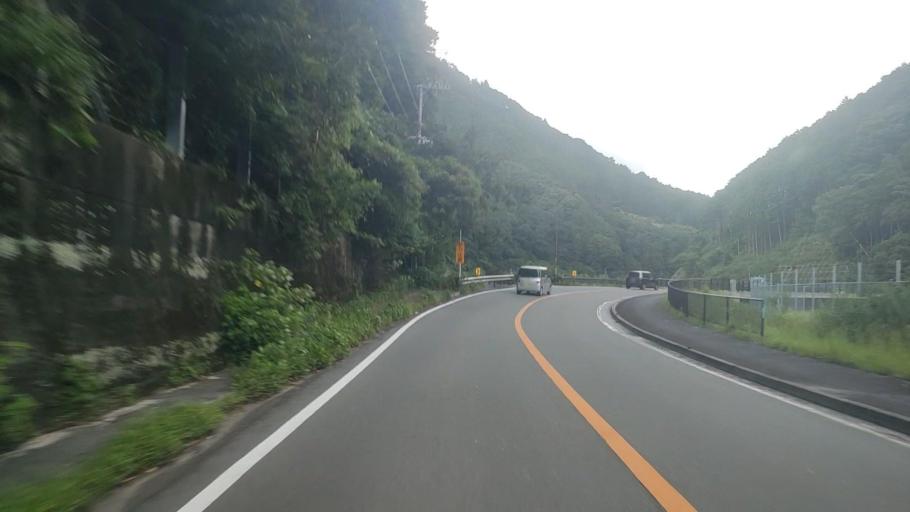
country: JP
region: Wakayama
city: Tanabe
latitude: 33.7713
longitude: 135.5000
